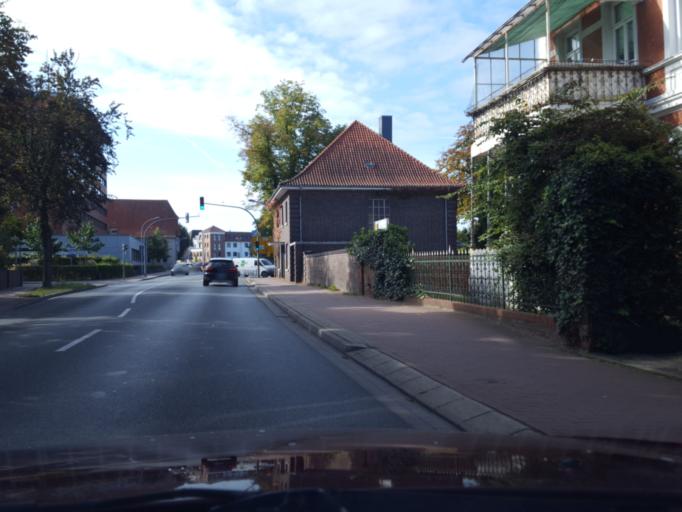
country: DE
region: Lower Saxony
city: Verden
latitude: 52.9264
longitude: 9.2295
